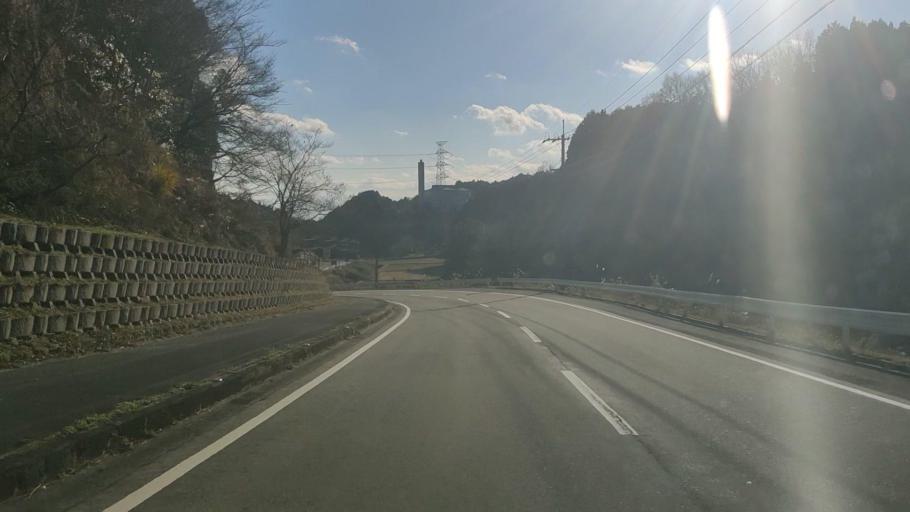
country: JP
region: Saga Prefecture
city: Kanzakimachi-kanzaki
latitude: 33.4033
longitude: 130.2726
